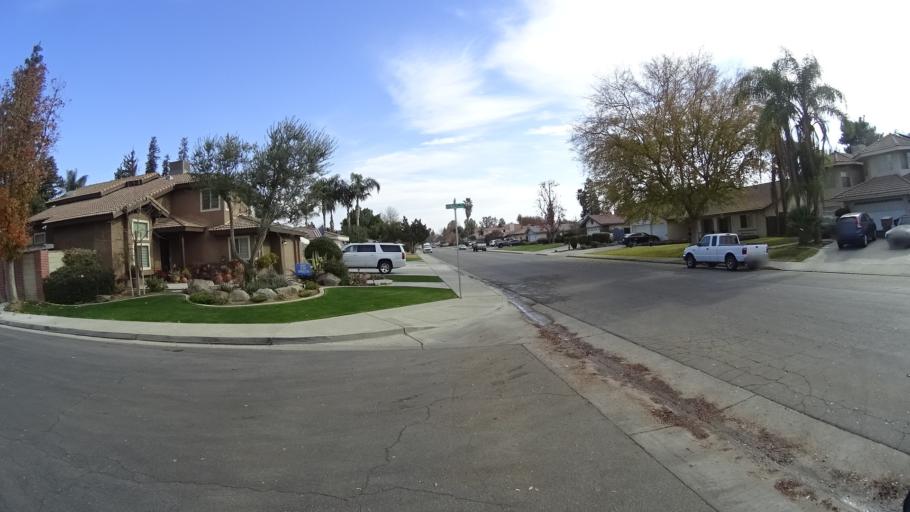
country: US
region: California
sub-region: Kern County
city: Greenacres
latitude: 35.4048
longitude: -119.0812
